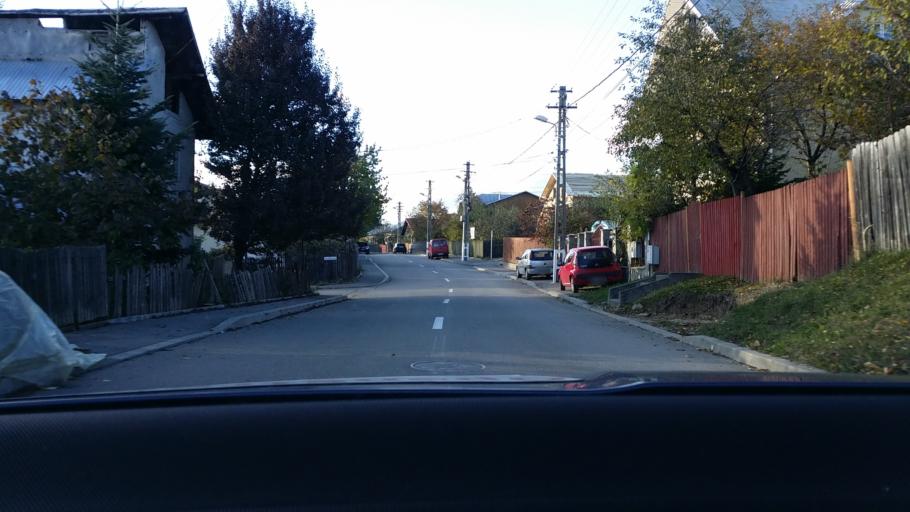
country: RO
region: Prahova
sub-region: Municipiul Campina
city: Campina
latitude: 45.1392
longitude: 25.7415
